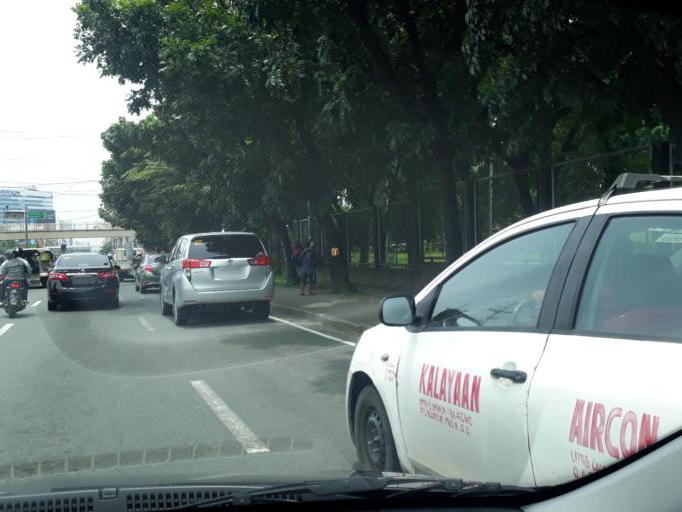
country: PH
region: Calabarzon
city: Bagong Pagasa
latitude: 14.6544
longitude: 121.0363
